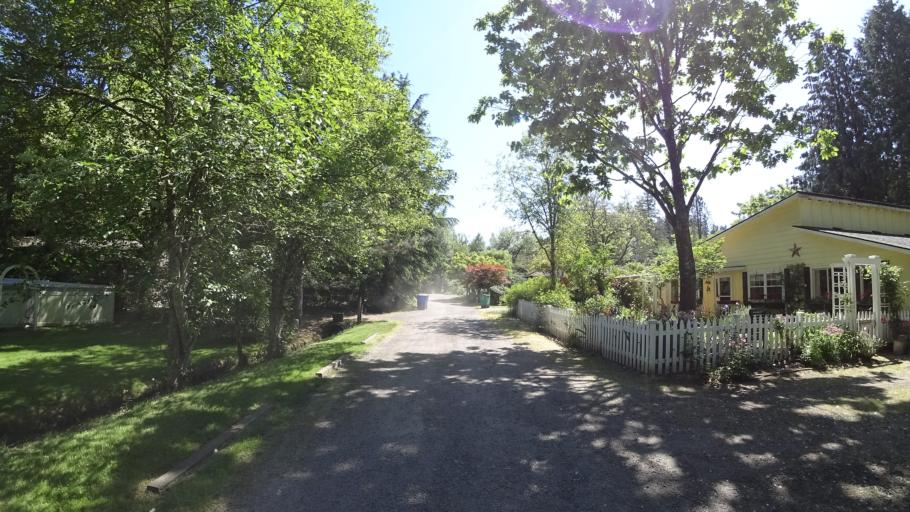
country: US
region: Oregon
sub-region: Washington County
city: Metzger
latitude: 45.4473
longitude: -122.7171
